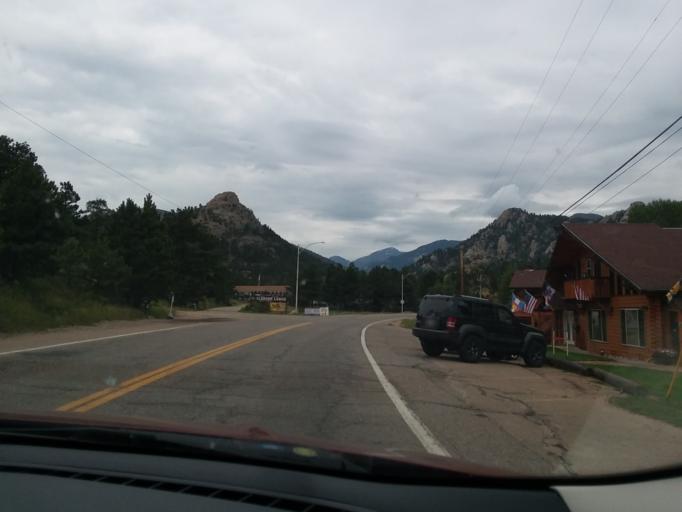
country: US
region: Colorado
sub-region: Larimer County
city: Estes Park
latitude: 40.3765
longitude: -105.5305
